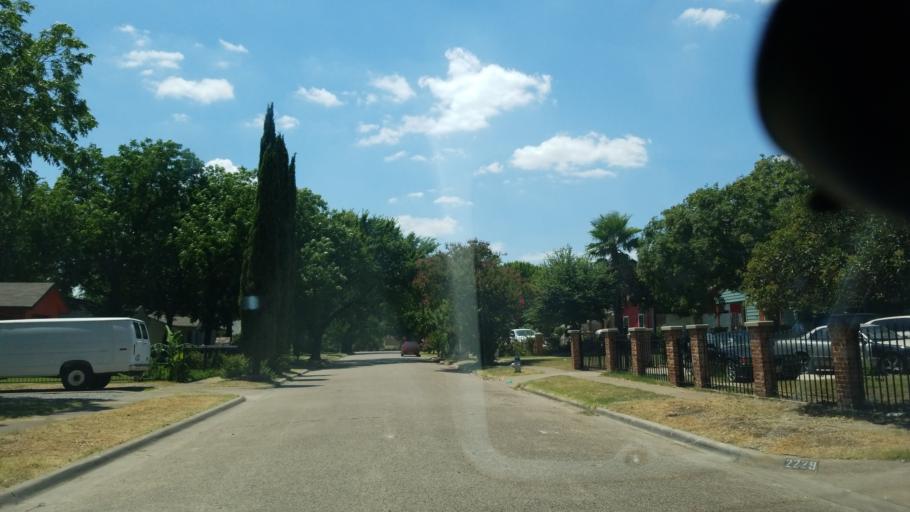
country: US
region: Texas
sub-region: Dallas County
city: Cockrell Hill
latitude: 32.7151
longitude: -96.8555
